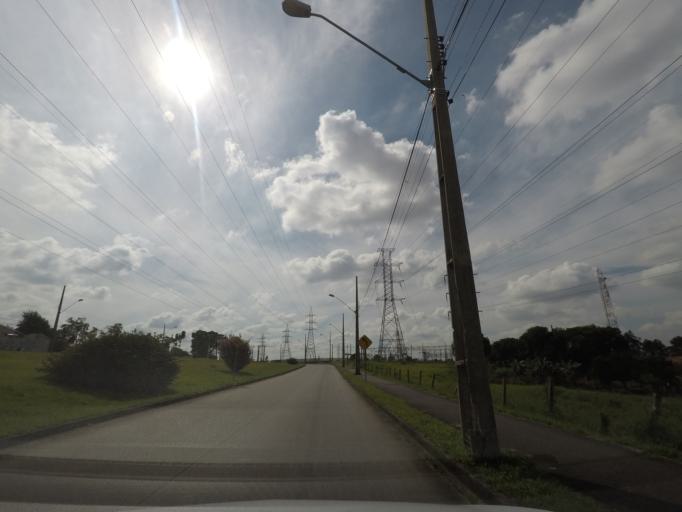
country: BR
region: Parana
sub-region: Pinhais
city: Pinhais
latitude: -25.4799
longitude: -49.2086
